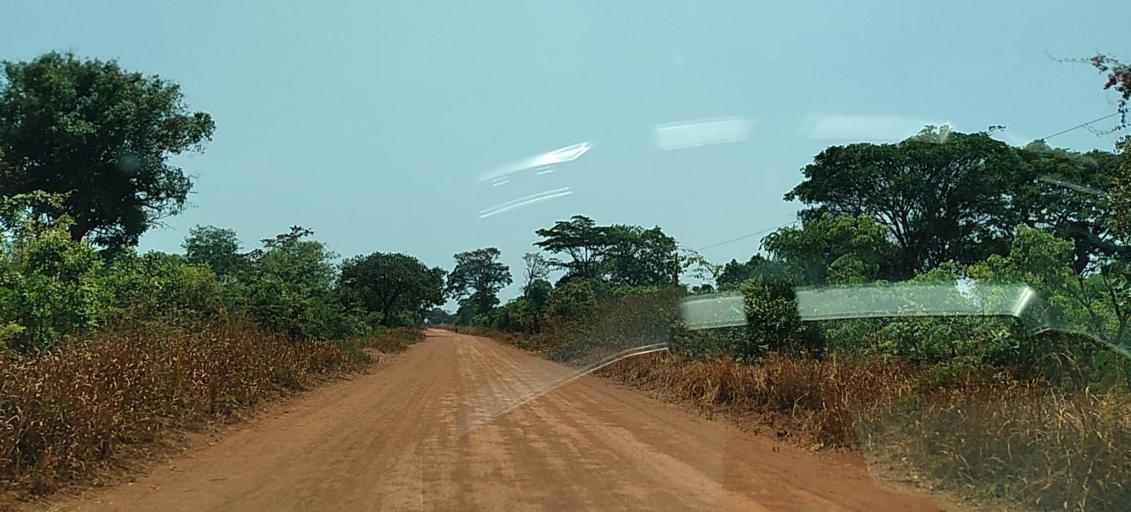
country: CD
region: Katanga
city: Kipushi
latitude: -11.9817
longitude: 26.8866
